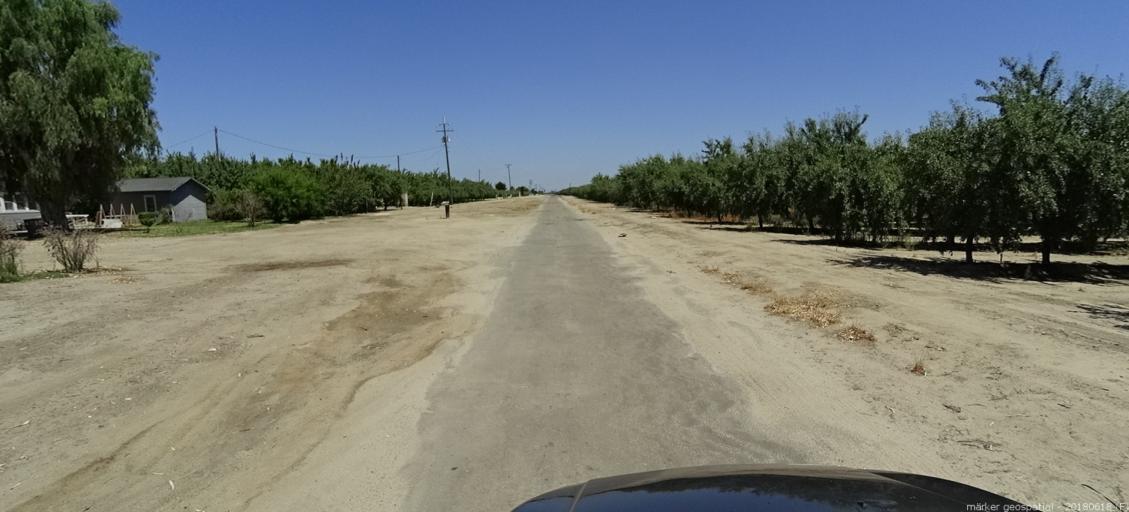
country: US
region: California
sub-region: Madera County
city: Parkwood
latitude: 36.8748
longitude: -120.1013
